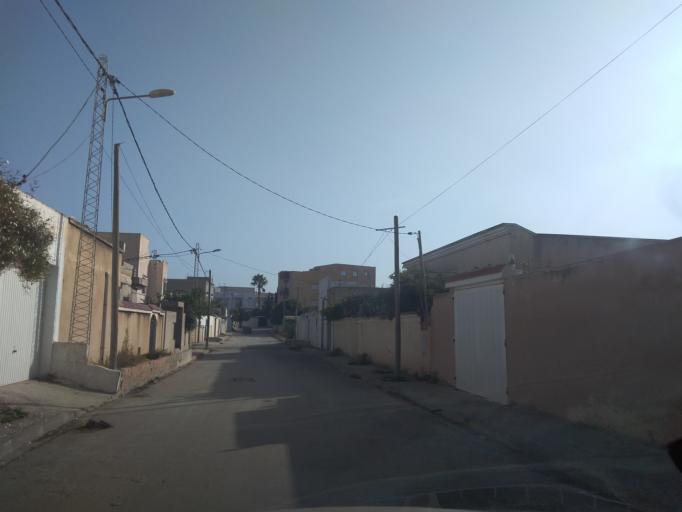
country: TN
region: Manouba
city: Manouba
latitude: 36.7932
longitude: 10.0865
